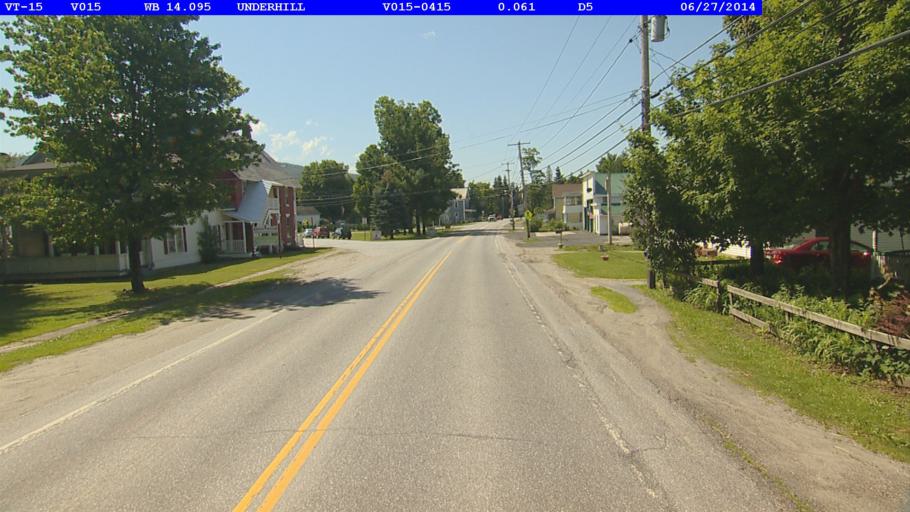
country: US
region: Vermont
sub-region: Chittenden County
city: Jericho
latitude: 44.5260
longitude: -72.9451
